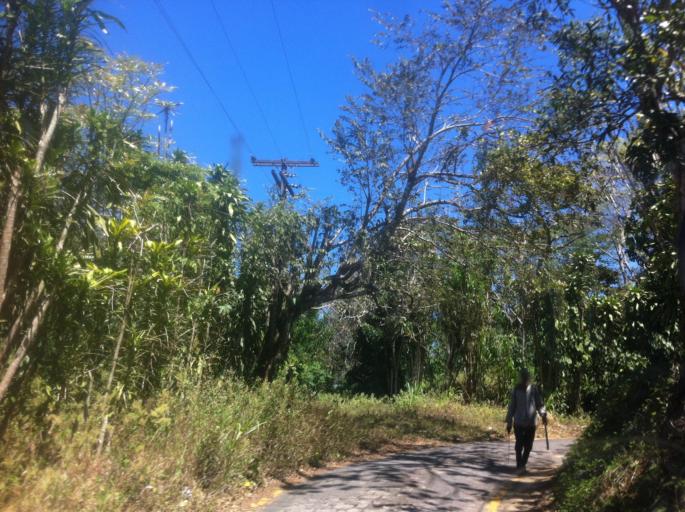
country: NI
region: Granada
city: Diriomo
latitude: 11.8388
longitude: -85.9921
